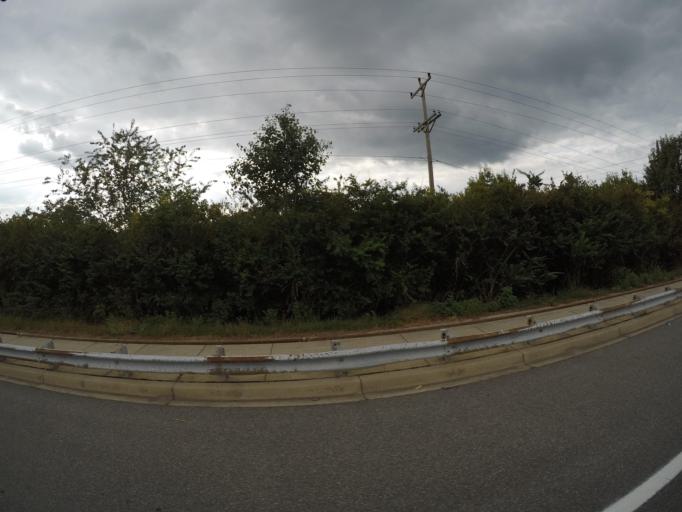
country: US
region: Delaware
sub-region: New Castle County
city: Brookside
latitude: 39.6767
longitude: -75.7290
